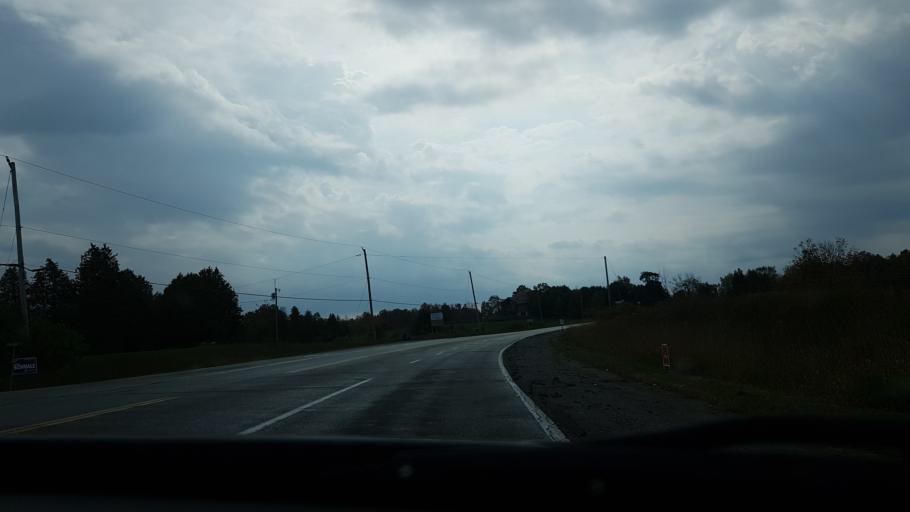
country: CA
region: Ontario
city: Omemee
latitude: 44.4903
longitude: -78.7461
